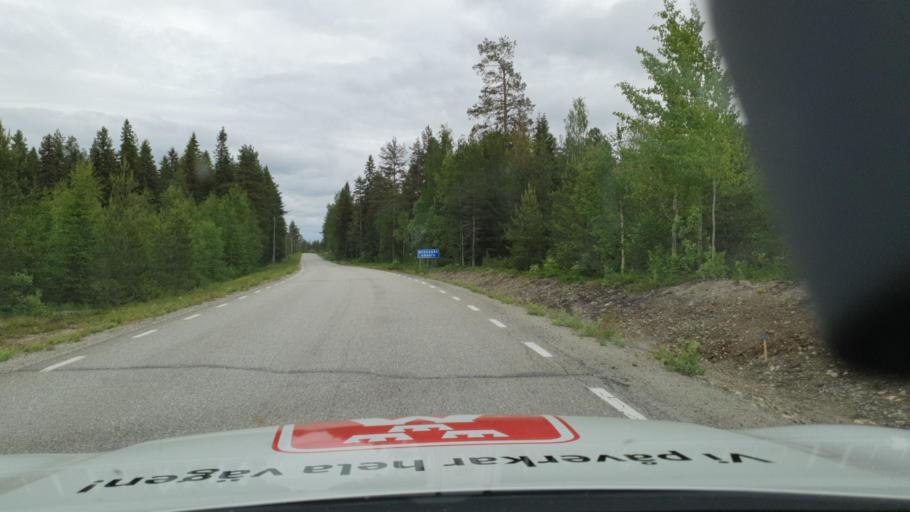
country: SE
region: Vaesterbotten
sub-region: Lycksele Kommun
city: Soderfors
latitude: 64.2954
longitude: 18.1757
